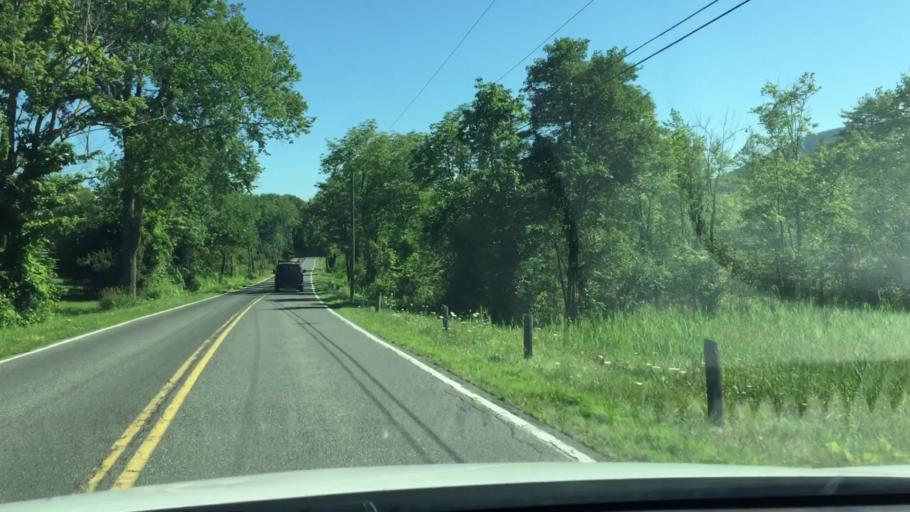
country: US
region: Massachusetts
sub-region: Berkshire County
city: Richmond
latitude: 42.3819
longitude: -73.3445
